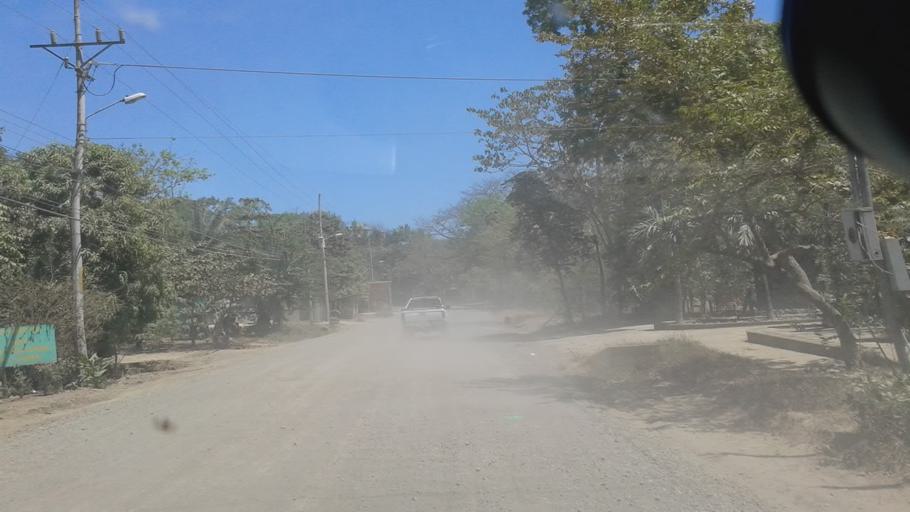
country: CR
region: Guanacaste
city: Samara
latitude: 9.9401
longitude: -85.6560
